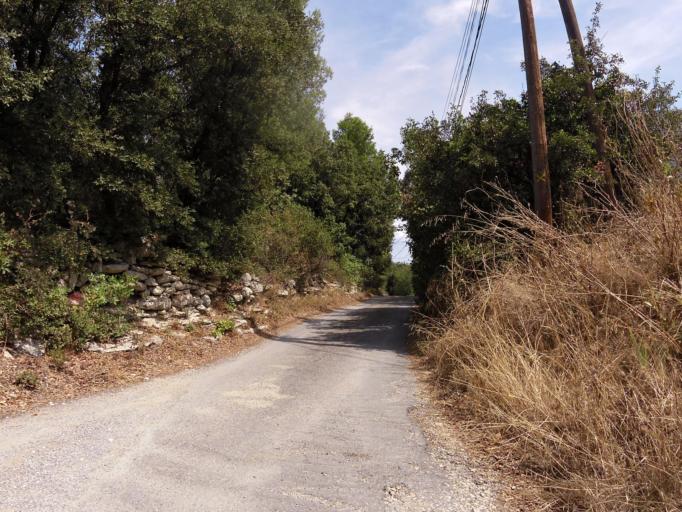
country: FR
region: Languedoc-Roussillon
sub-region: Departement du Gard
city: Villevieille
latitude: 43.7680
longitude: 4.1174
